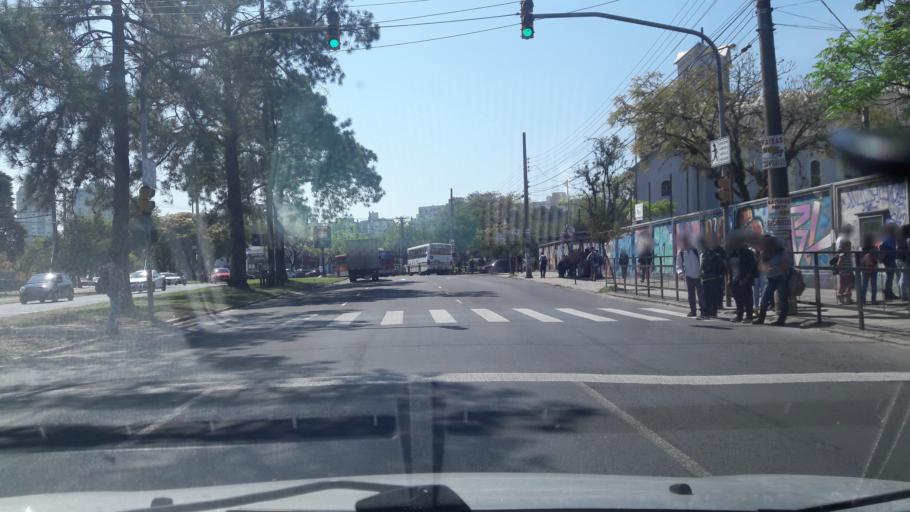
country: BR
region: Rio Grande do Sul
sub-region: Guaiba
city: Guaiba
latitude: -30.1109
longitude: -51.2546
